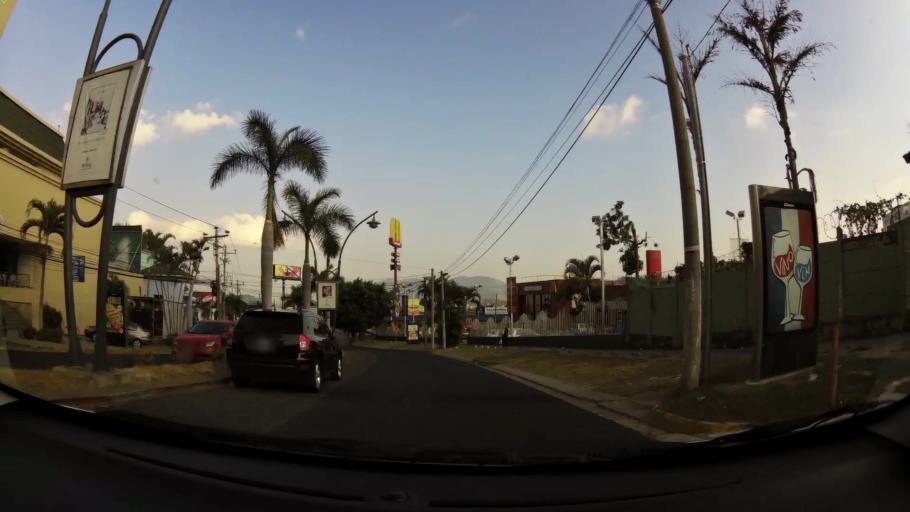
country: SV
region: La Libertad
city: Antiguo Cuscatlan
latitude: 13.6925
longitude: -89.2377
